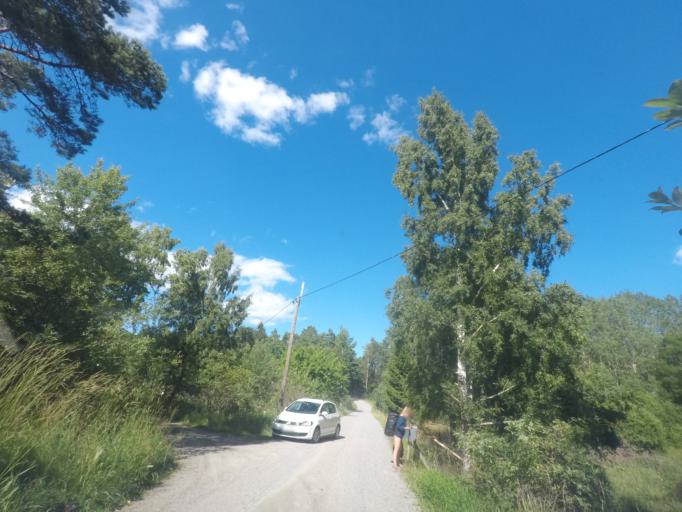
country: SE
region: Stockholm
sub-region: Norrtalje Kommun
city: Arno
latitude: 60.2125
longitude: 18.7304
